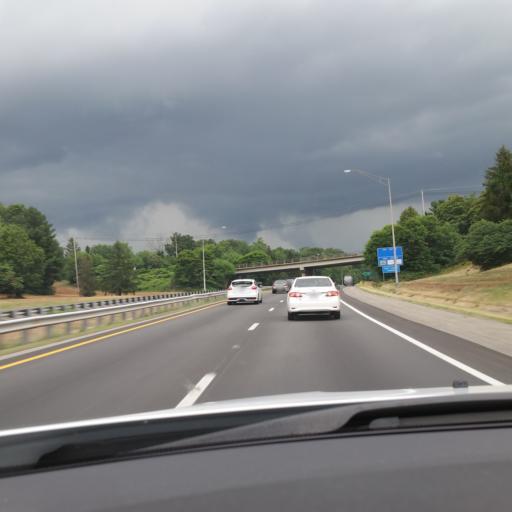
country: US
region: North Carolina
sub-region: Buncombe County
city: Woodfin
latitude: 35.6294
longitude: -82.5803
